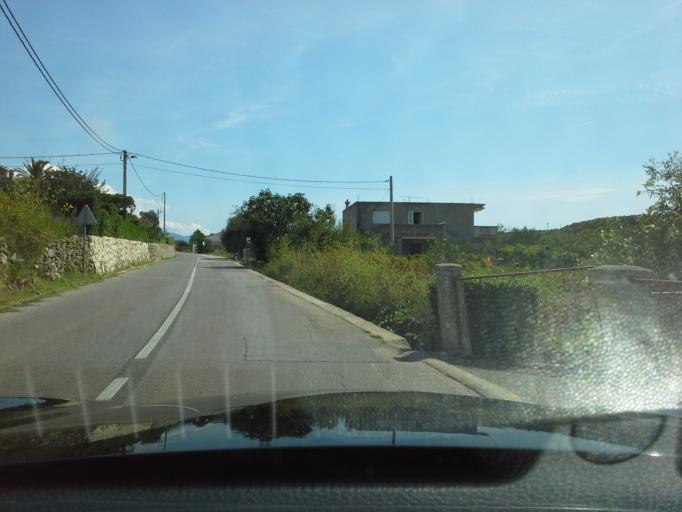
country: HR
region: Primorsko-Goranska
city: Kampor
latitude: 44.7832
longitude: 14.7154
